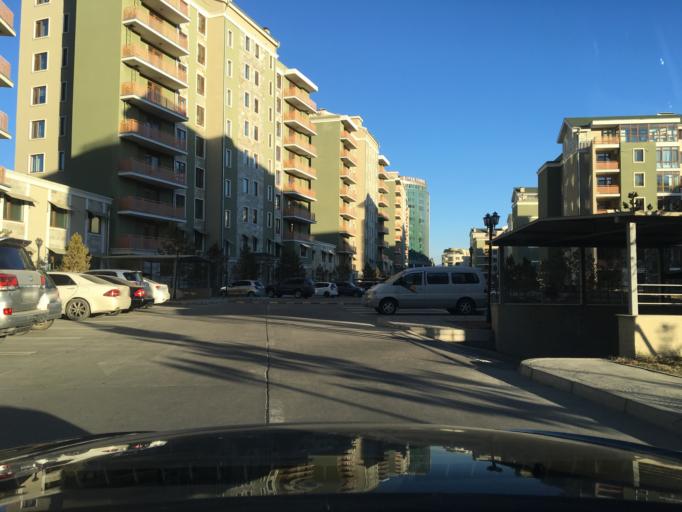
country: MN
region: Ulaanbaatar
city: Ulaanbaatar
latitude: 47.8902
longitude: 106.9288
